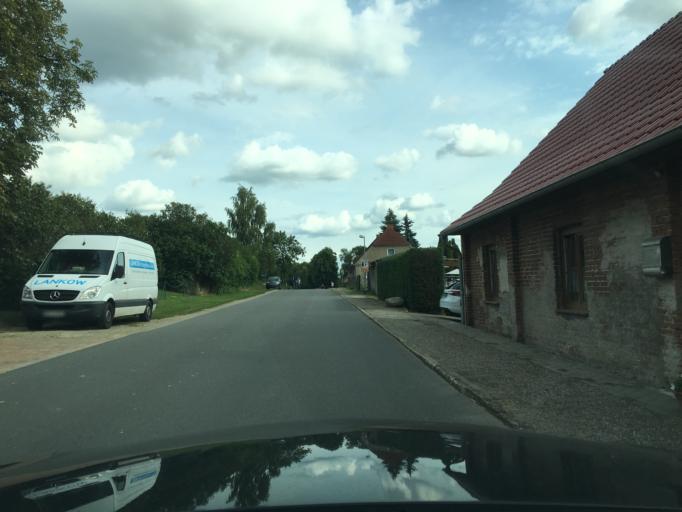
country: DE
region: Mecklenburg-Vorpommern
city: Mollenhagen
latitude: 53.4828
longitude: 12.9609
